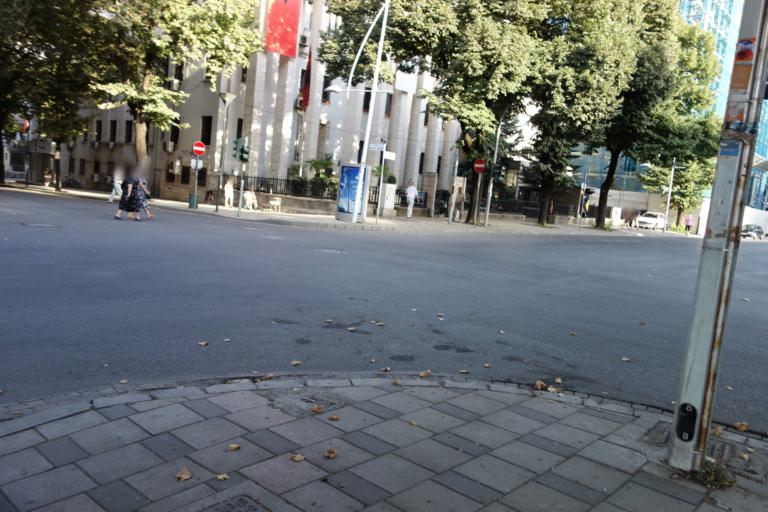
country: AL
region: Tirane
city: Tirana
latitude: 41.3255
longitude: 19.8172
